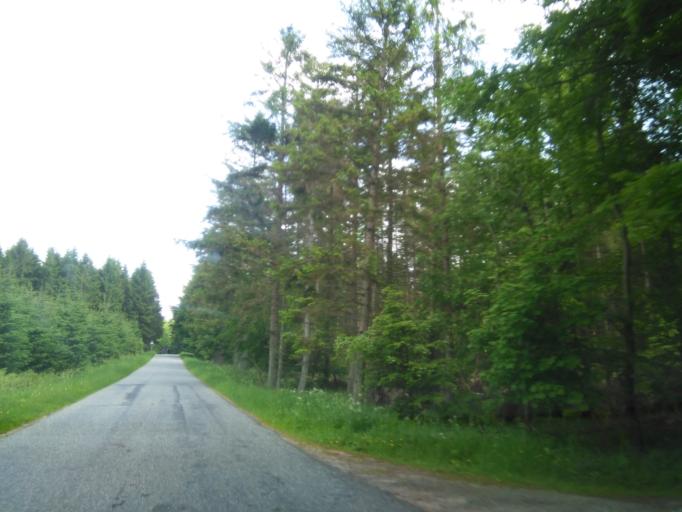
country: DK
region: Central Jutland
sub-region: Skanderborg Kommune
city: Galten
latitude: 56.2248
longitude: 9.9273
